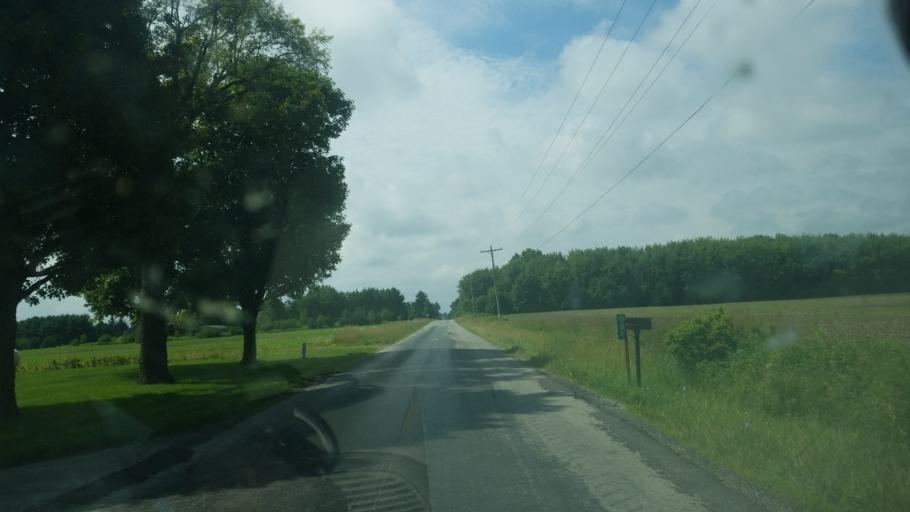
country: US
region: Ohio
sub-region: Licking County
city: Johnstown
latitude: 40.2049
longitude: -82.7561
